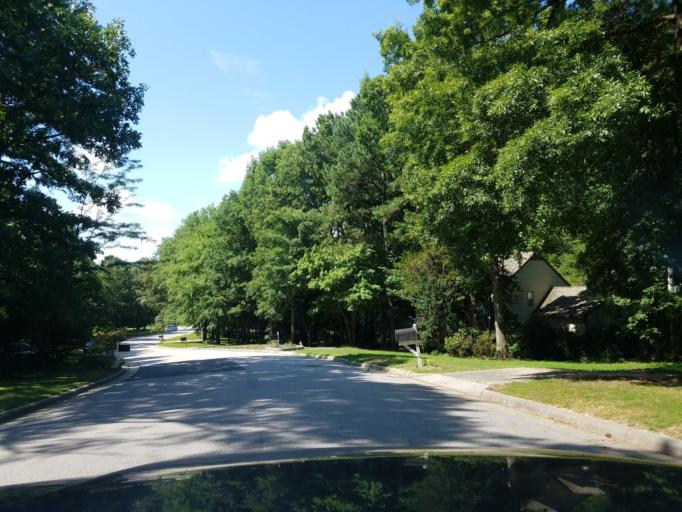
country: US
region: North Carolina
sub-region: Durham County
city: Durham
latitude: 35.9204
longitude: -78.9399
